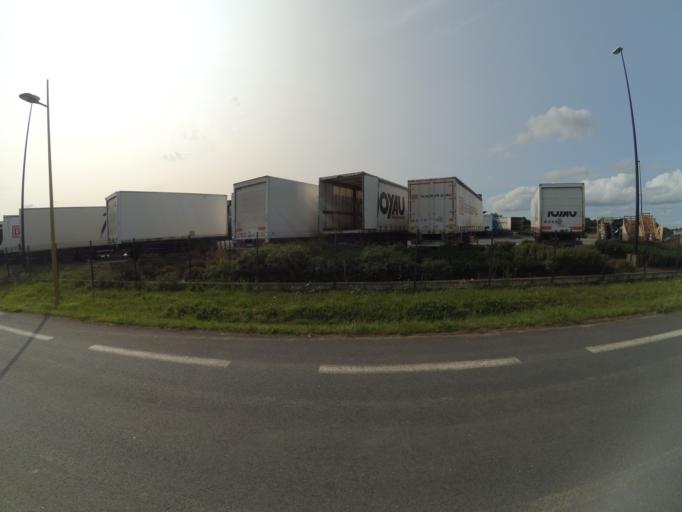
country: FR
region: Pays de la Loire
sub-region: Departement de la Vendee
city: Bouffere
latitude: 46.9465
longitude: -1.3459
